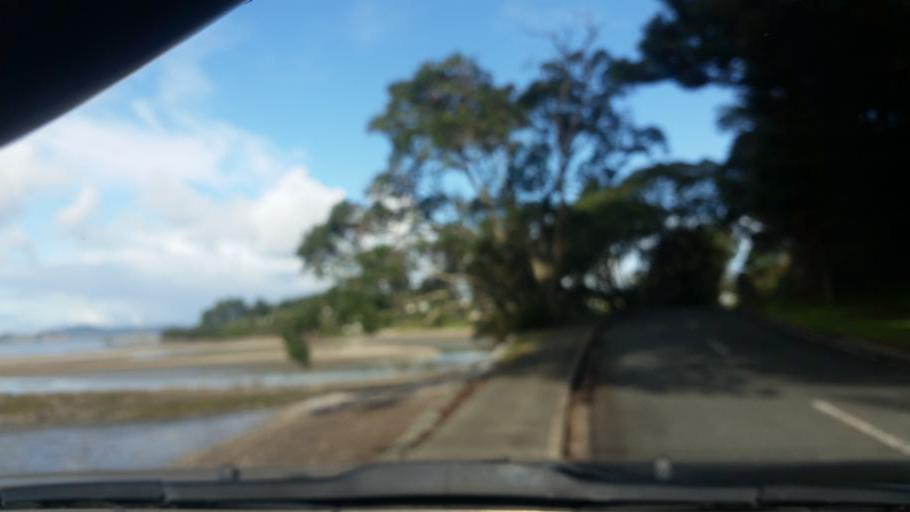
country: NZ
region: Auckland
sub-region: Auckland
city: Wellsford
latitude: -36.2512
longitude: 174.2480
